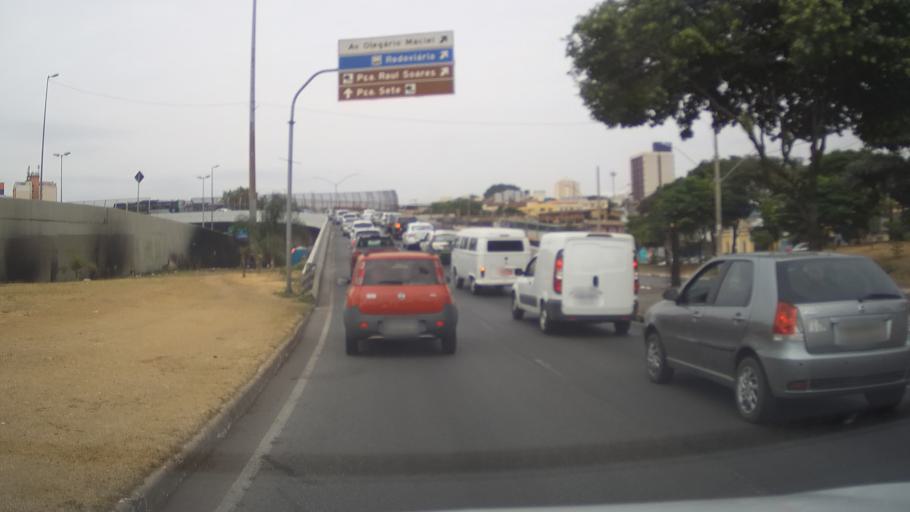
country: BR
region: Minas Gerais
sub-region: Belo Horizonte
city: Belo Horizonte
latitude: -19.9124
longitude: -43.9429
